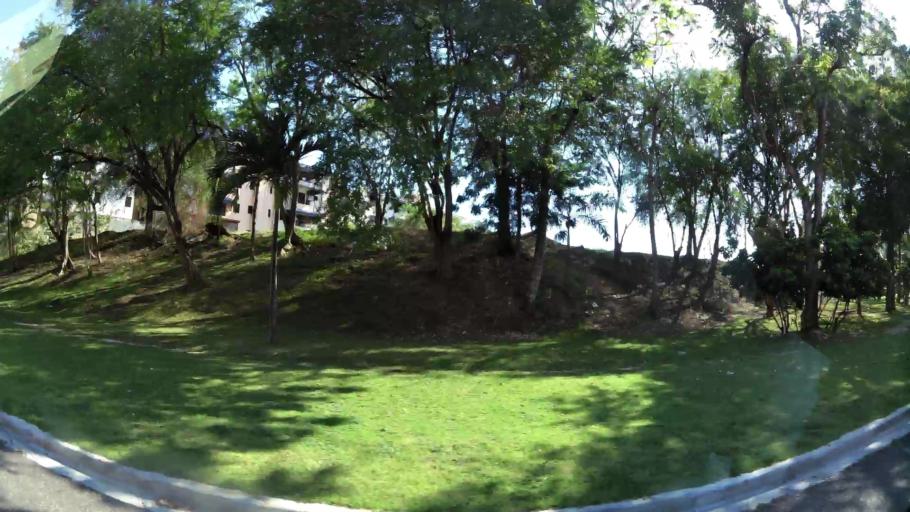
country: DO
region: Nacional
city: Bella Vista
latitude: 18.4601
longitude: -69.9834
